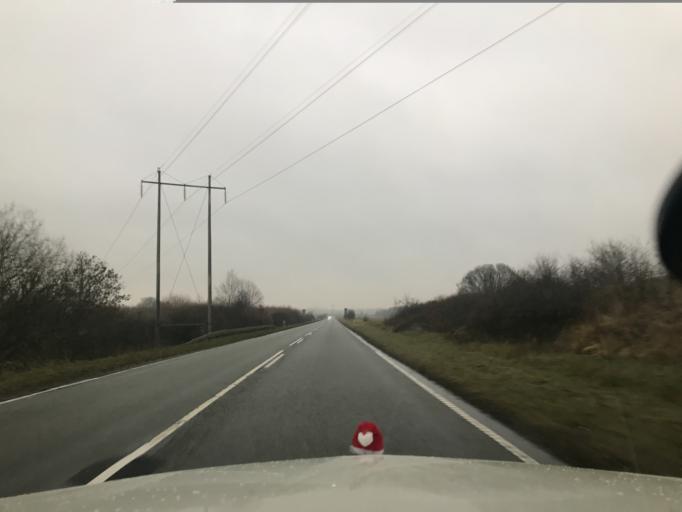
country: DK
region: South Denmark
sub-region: Aabenraa Kommune
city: Aabenraa
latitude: 55.0024
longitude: 9.3882
